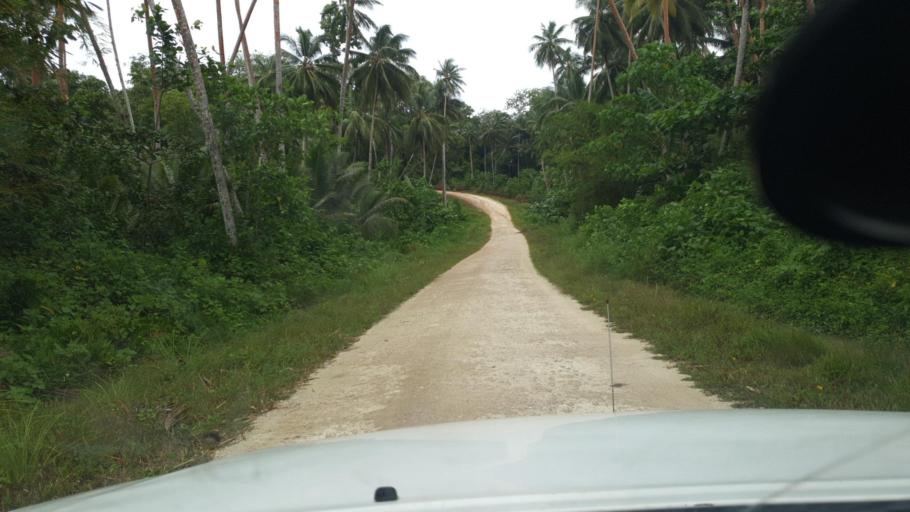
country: SB
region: Western Province
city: Gizo
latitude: -8.0459
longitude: 156.7742
